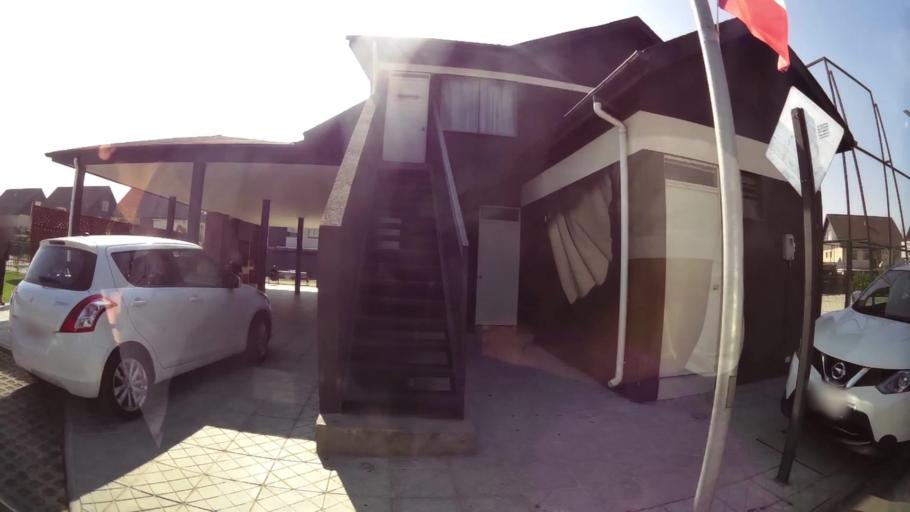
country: CL
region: Santiago Metropolitan
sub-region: Provincia de Santiago
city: Lo Prado
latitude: -33.4815
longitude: -70.7656
